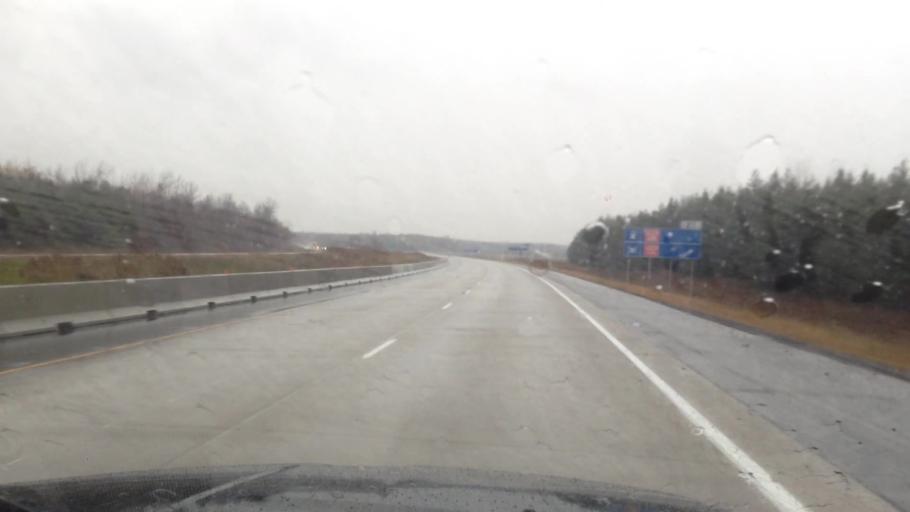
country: CA
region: Ontario
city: Hawkesbury
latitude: 45.4505
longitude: -74.7031
